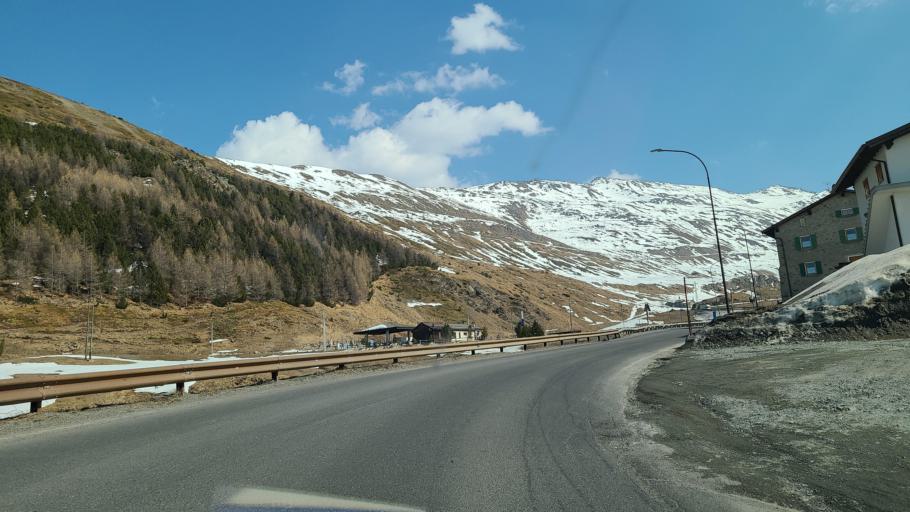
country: IT
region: Lombardy
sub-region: Provincia di Sondrio
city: Livigno
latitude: 46.5183
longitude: 10.1844
